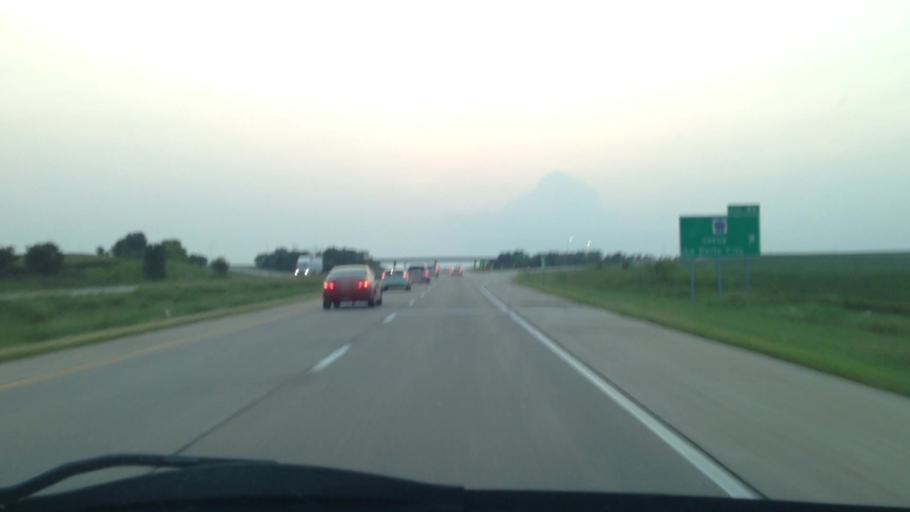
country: US
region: Iowa
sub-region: Buchanan County
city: Jesup
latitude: 42.3514
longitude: -92.0575
